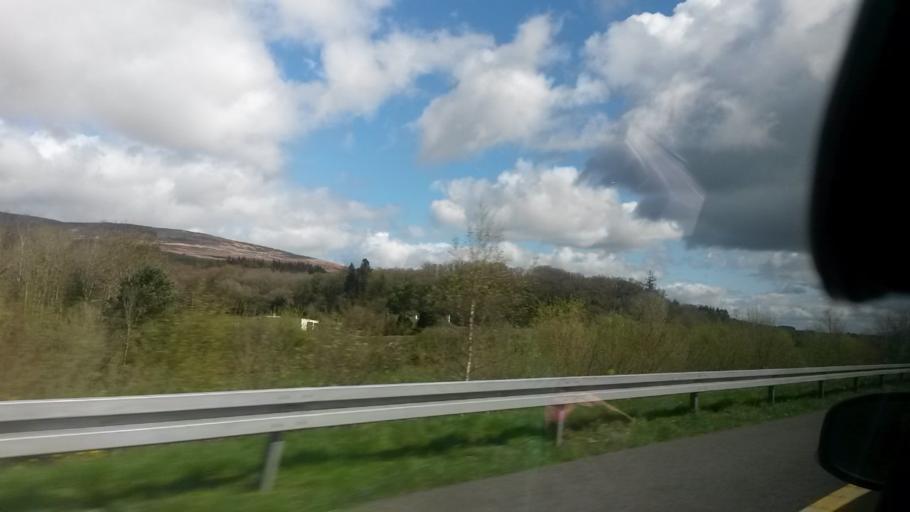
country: IE
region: Munster
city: Tipperary
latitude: 52.3182
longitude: -8.1085
